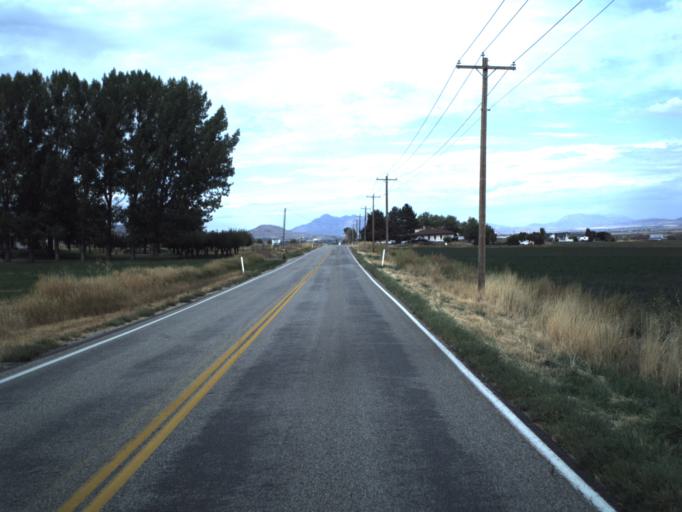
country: US
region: Utah
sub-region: Cache County
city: Wellsville
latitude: 41.6540
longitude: -111.9421
